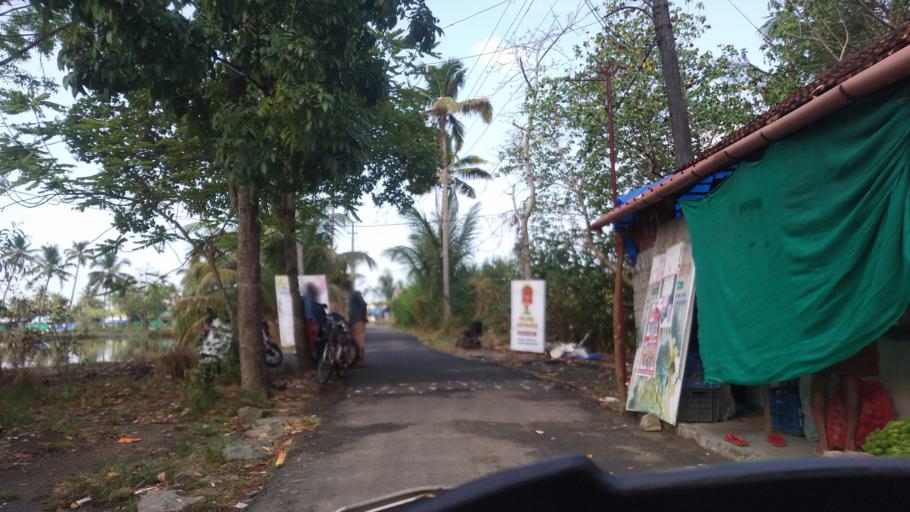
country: IN
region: Kerala
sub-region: Thrissur District
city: Kodungallur
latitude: 10.1359
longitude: 76.2120
